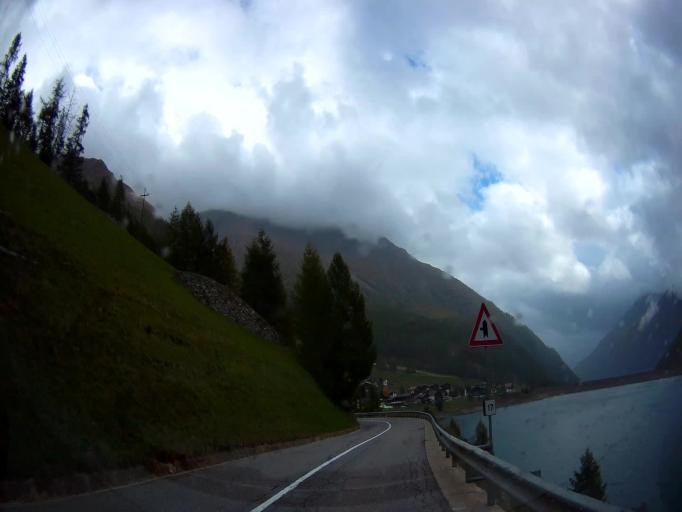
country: IT
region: Trentino-Alto Adige
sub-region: Bolzano
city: Senales
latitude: 46.7387
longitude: 10.8414
